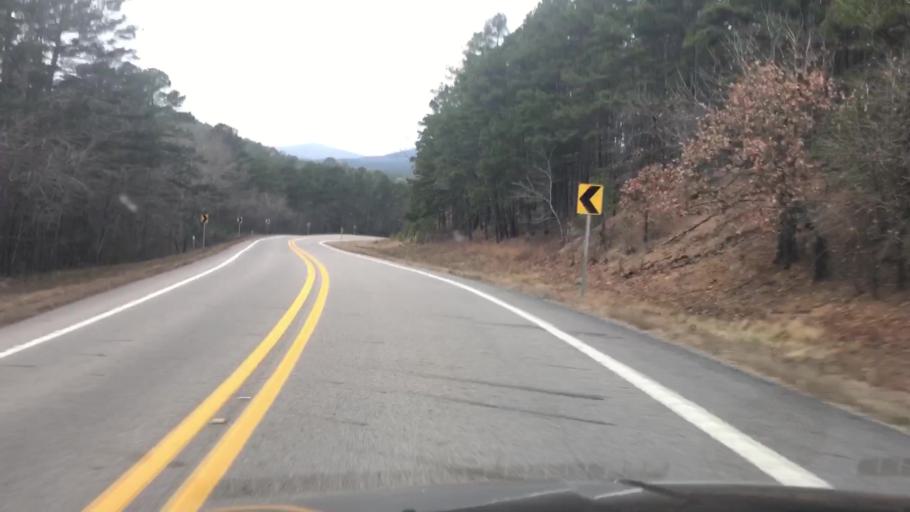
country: US
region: Arkansas
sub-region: Montgomery County
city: Mount Ida
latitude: 34.6836
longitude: -93.7991
